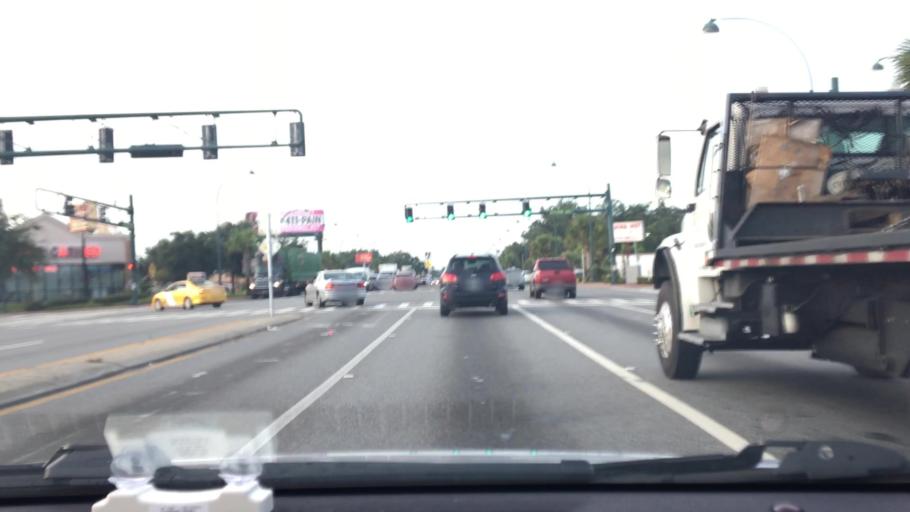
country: US
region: Florida
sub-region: Orange County
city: Holden Heights
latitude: 28.4949
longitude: -81.3969
